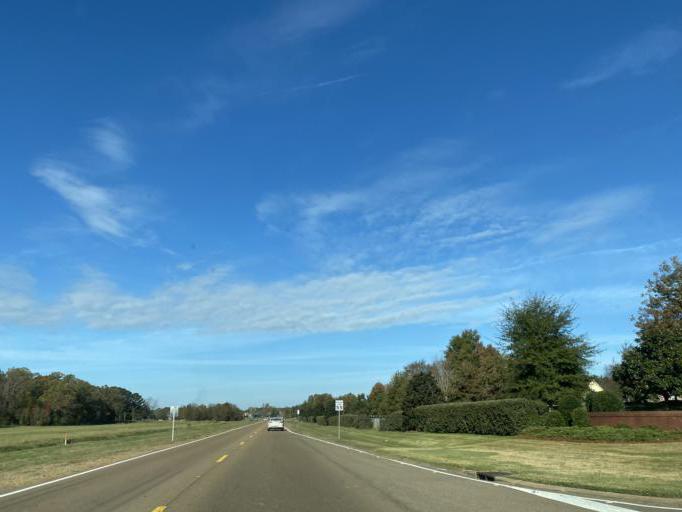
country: US
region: Mississippi
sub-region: Madison County
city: Madison
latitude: 32.4765
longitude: -90.1535
